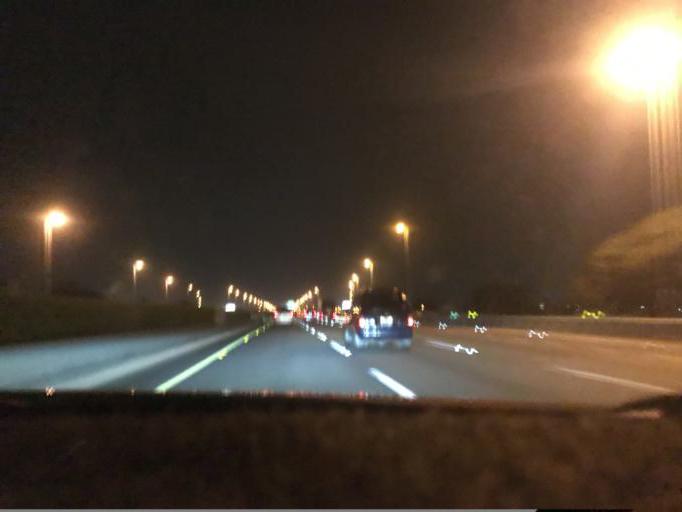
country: TW
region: Taiwan
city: Fengyuan
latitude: 24.3910
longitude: 120.6683
